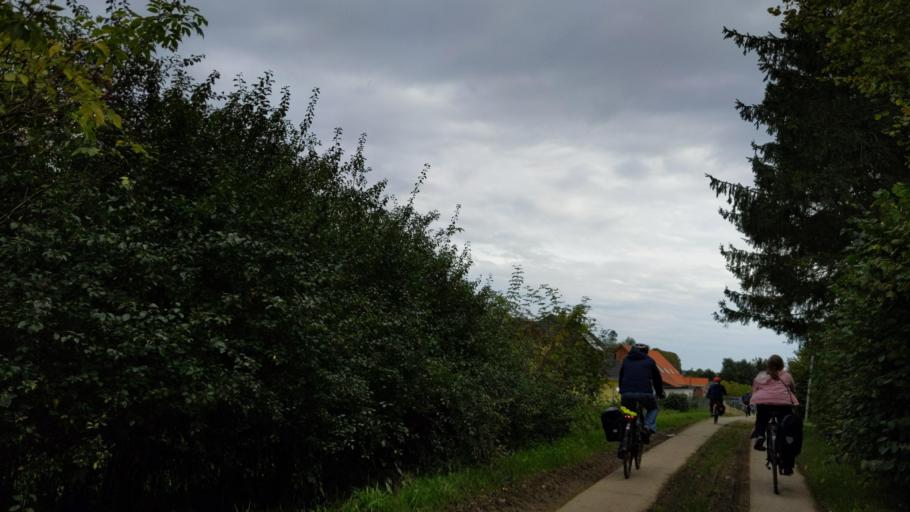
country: DE
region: Mecklenburg-Vorpommern
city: Schlagsdorf
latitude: 53.7311
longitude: 10.8171
